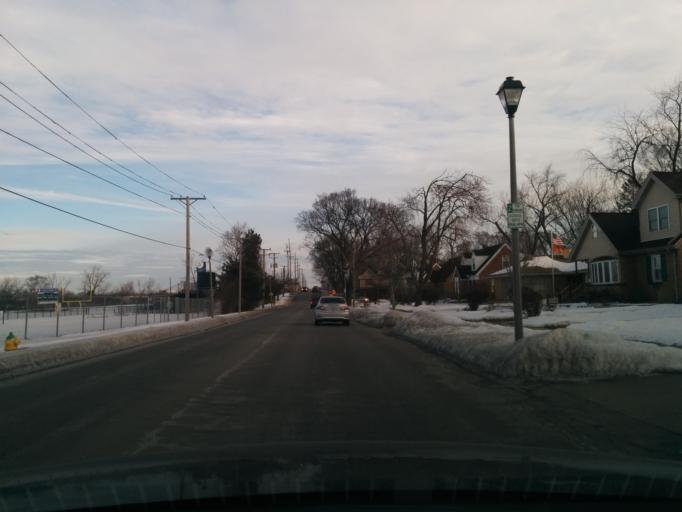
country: US
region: Illinois
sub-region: DuPage County
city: Elmhurst
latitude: 41.8964
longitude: -87.9593
